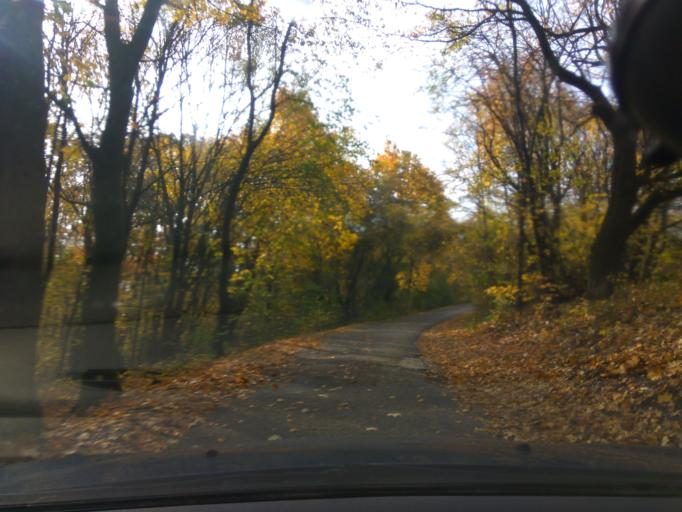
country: SK
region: Trnavsky
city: Vrbove
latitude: 48.6803
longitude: 17.7111
